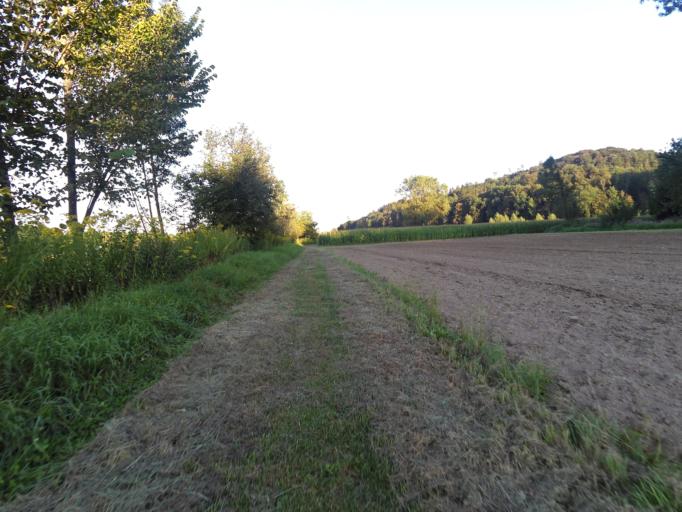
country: CH
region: Thurgau
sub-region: Weinfelden District
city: Wigoltingen
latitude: 47.5819
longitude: 9.0161
